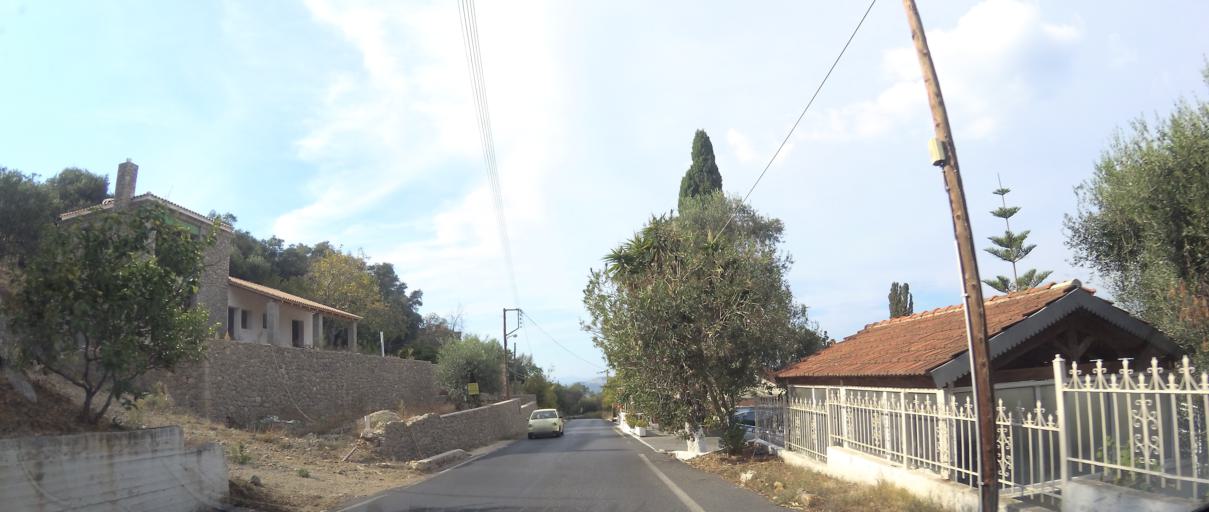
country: GR
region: Ionian Islands
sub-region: Nomos Kerkyras
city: Kynopiastes
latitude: 39.5536
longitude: 19.8616
